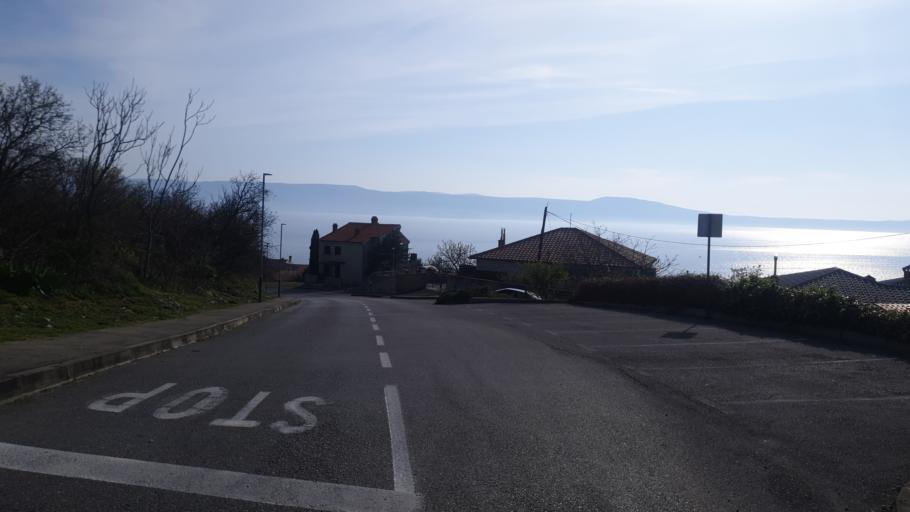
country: HR
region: Primorsko-Goranska
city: Novi Vinodolski
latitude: 45.1295
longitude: 14.7947
